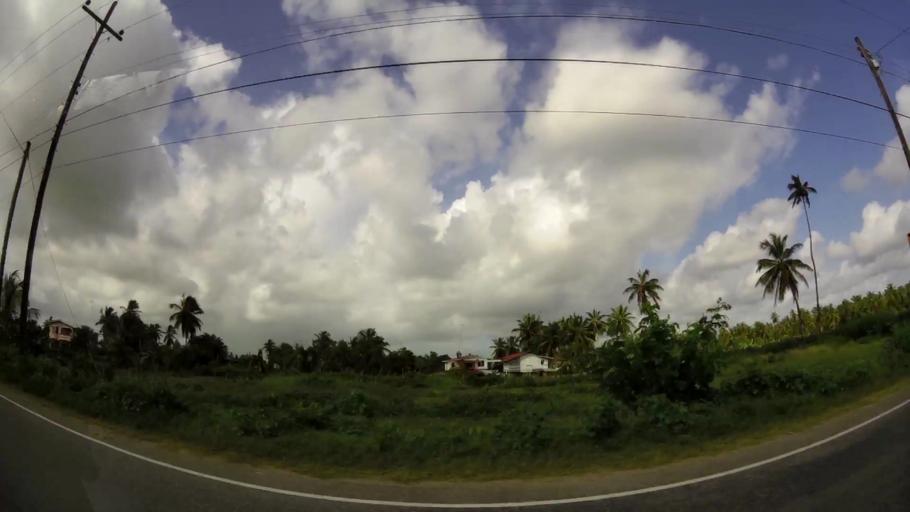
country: GY
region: Demerara-Mahaica
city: Mahaica Village
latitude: 6.6795
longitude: -57.9253
